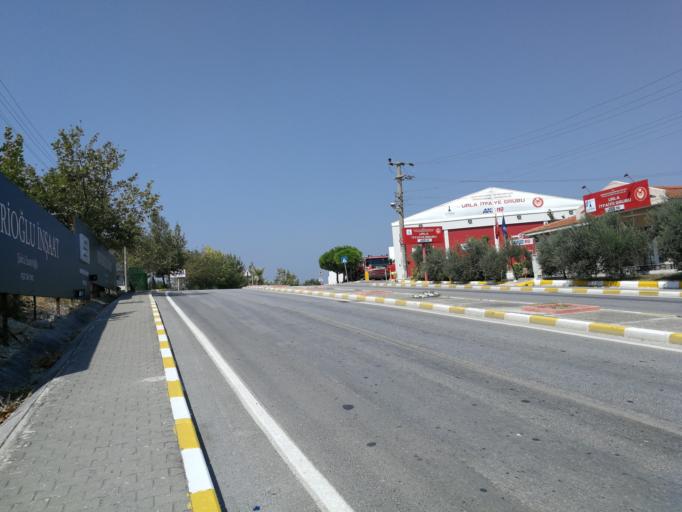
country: TR
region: Izmir
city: Urla
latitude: 38.3267
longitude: 26.7717
